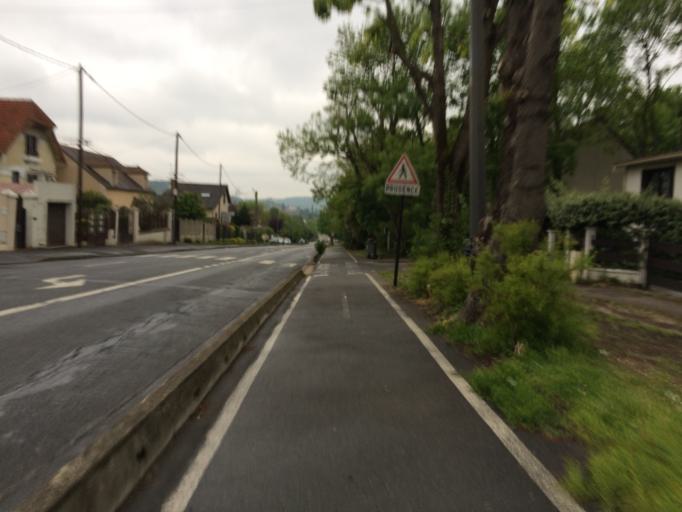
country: FR
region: Ile-de-France
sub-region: Departement de l'Essonne
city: Palaiseau
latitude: 48.7317
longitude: 2.2427
